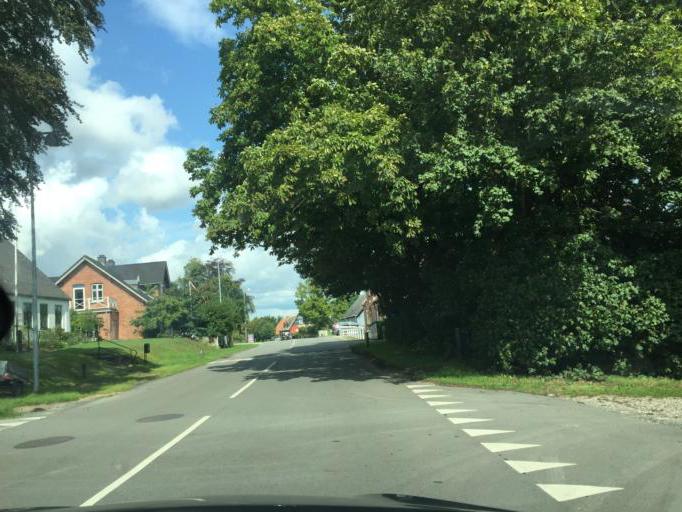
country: DK
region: South Denmark
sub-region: Odense Kommune
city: Stige
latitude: 55.4590
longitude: 10.3778
